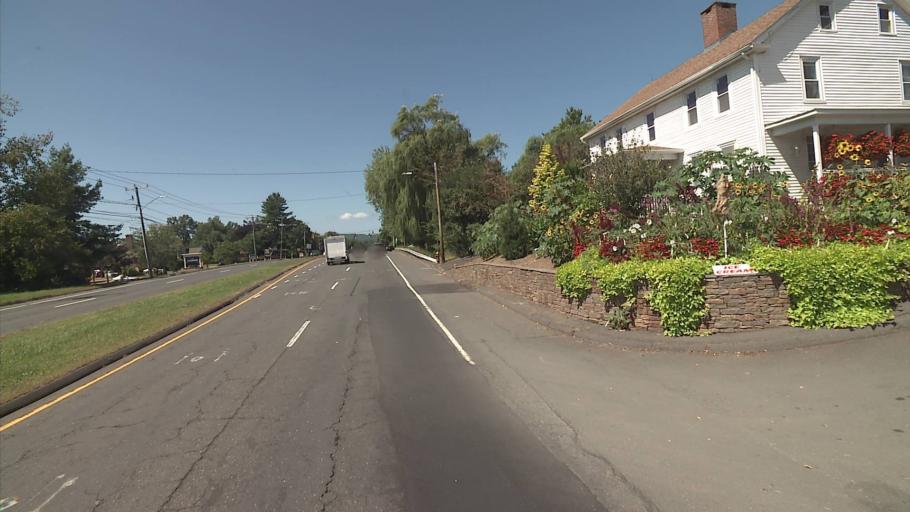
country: US
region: Connecticut
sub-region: Hartford County
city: Blue Hills
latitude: 41.8171
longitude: -72.7327
